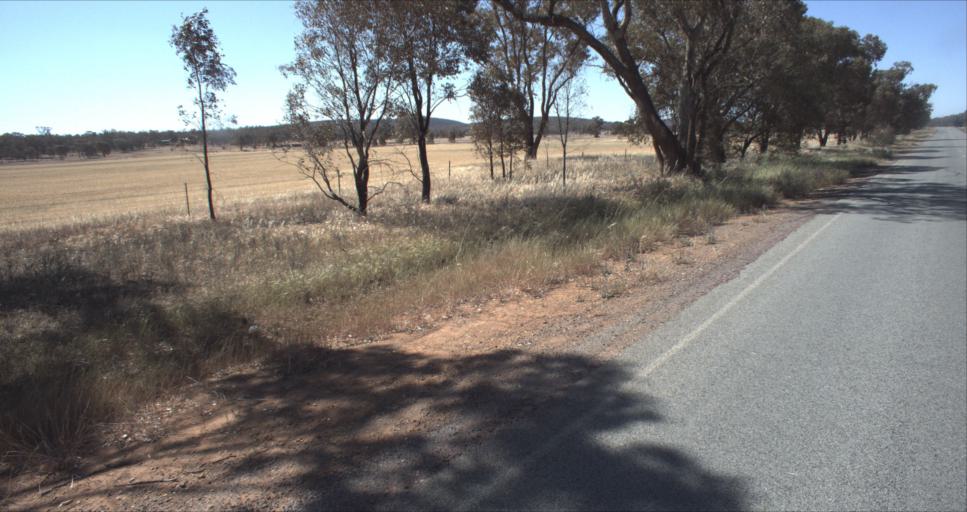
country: AU
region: New South Wales
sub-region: Leeton
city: Leeton
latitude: -34.4899
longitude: 146.4666
